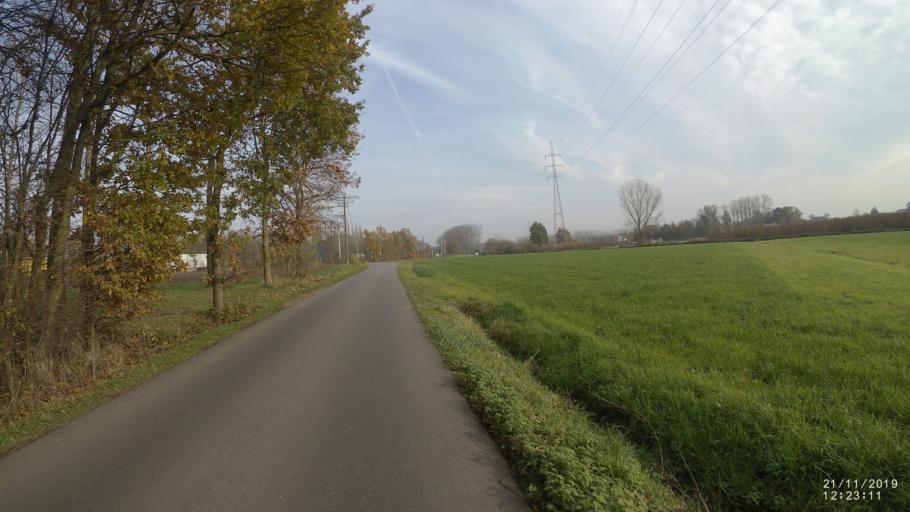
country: BE
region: Flanders
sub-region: Provincie Limburg
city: Alken
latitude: 50.8625
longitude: 5.2652
